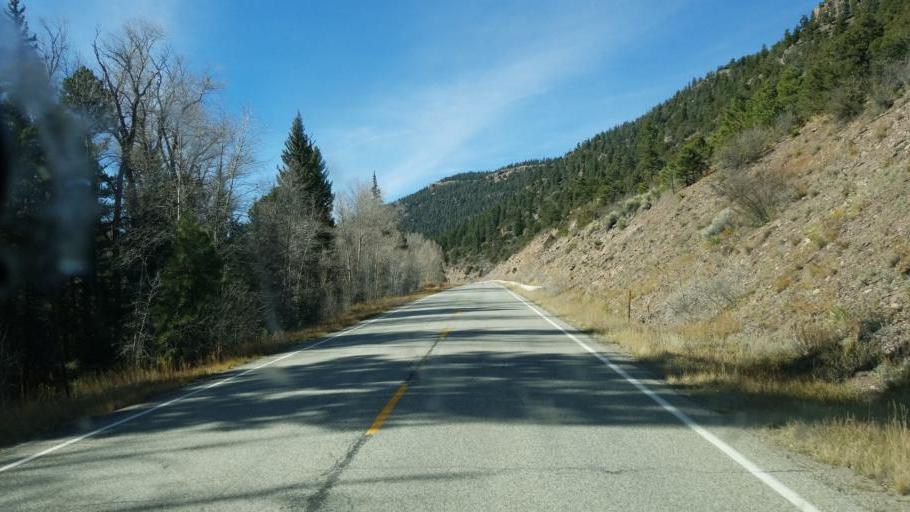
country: US
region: Colorado
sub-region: Conejos County
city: Conejos
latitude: 37.0698
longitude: -106.2531
